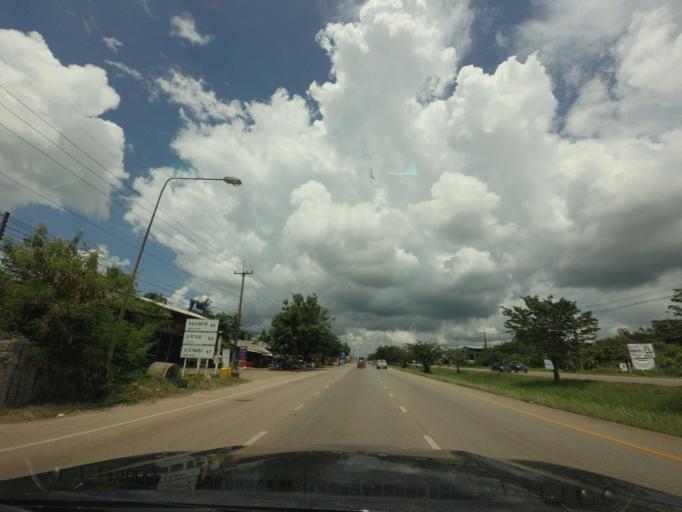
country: TH
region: Changwat Udon Thani
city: Udon Thani
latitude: 17.5274
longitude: 102.7994
